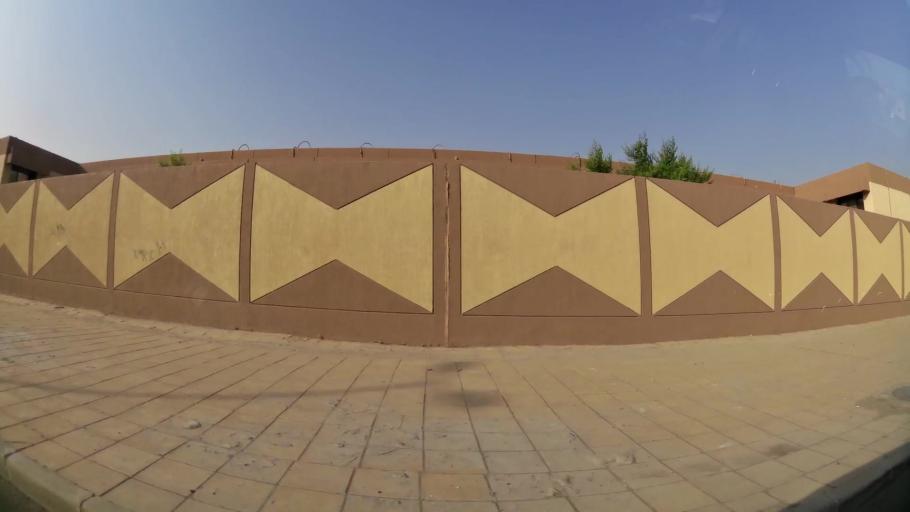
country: KW
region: Muhafazat Hawalli
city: Salwa
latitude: 29.2834
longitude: 48.0688
